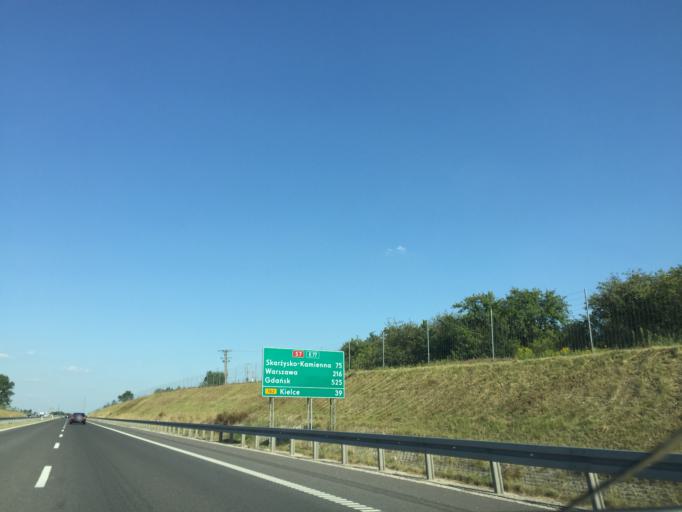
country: PL
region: Swietokrzyskie
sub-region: Powiat jedrzejowski
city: Jedrzejow
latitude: 50.6246
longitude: 20.2950
